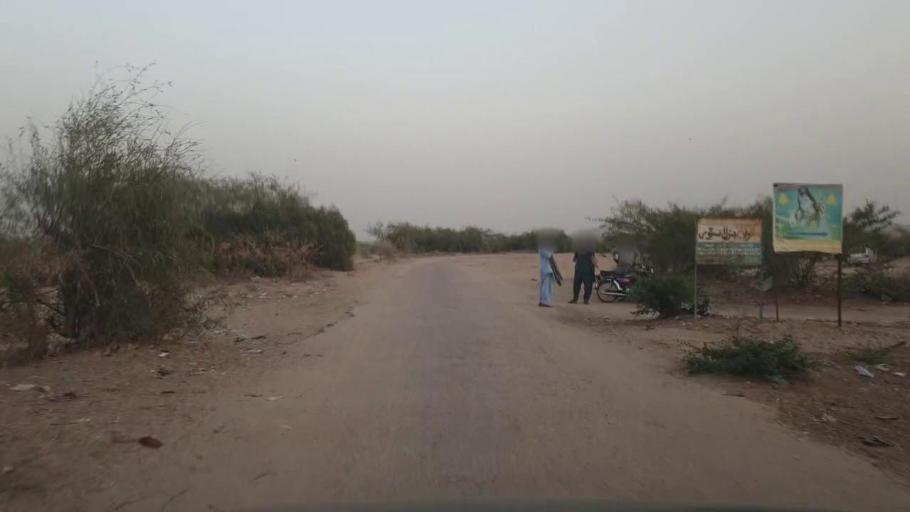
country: PK
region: Sindh
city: Chor
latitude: 25.5137
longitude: 69.8141
